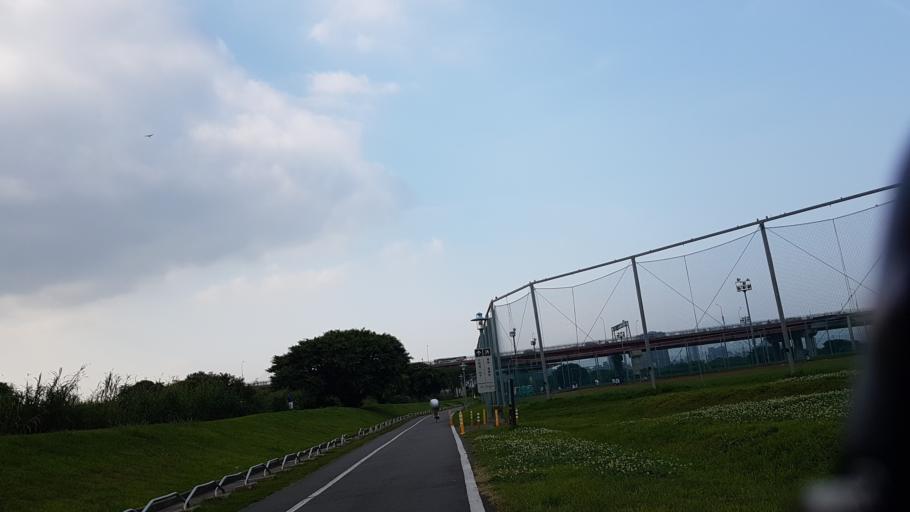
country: TW
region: Taipei
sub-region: Taipei
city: Banqiao
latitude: 25.0334
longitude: 121.4863
